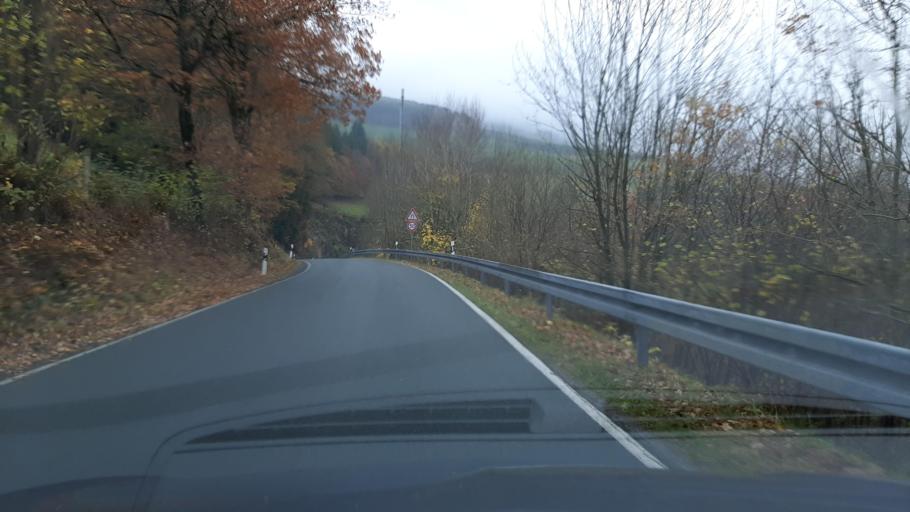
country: DE
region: North Rhine-Westphalia
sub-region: Regierungsbezirk Arnsberg
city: Olsberg
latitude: 51.2851
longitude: 8.4827
